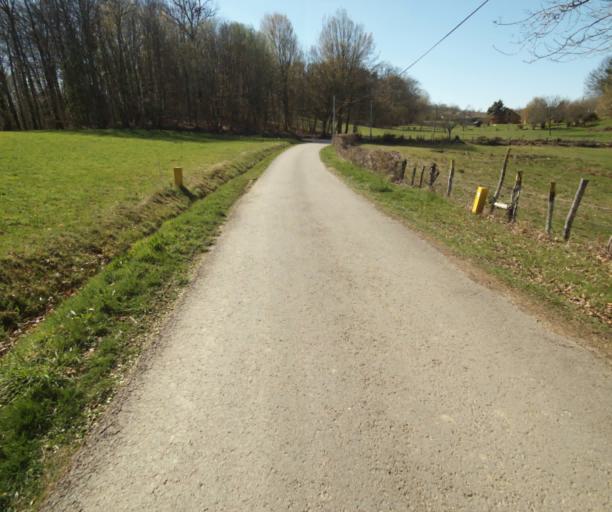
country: FR
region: Limousin
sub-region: Departement de la Correze
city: Chameyrat
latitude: 45.2524
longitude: 1.7075
